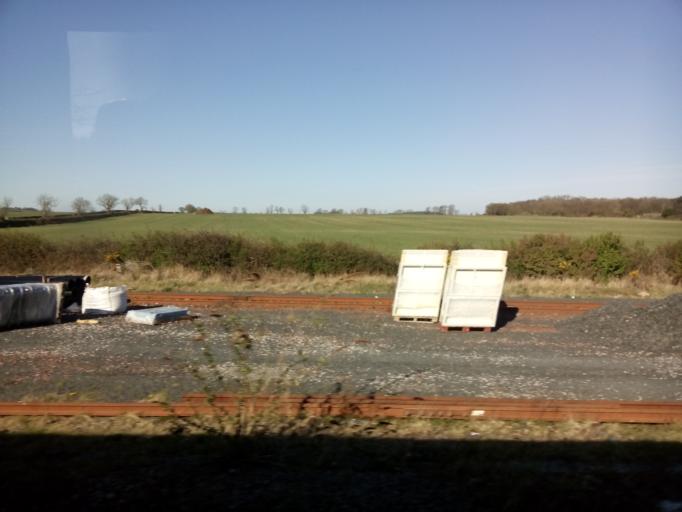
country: GB
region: England
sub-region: Northumberland
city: Acklington
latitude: 55.2658
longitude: -1.6519
